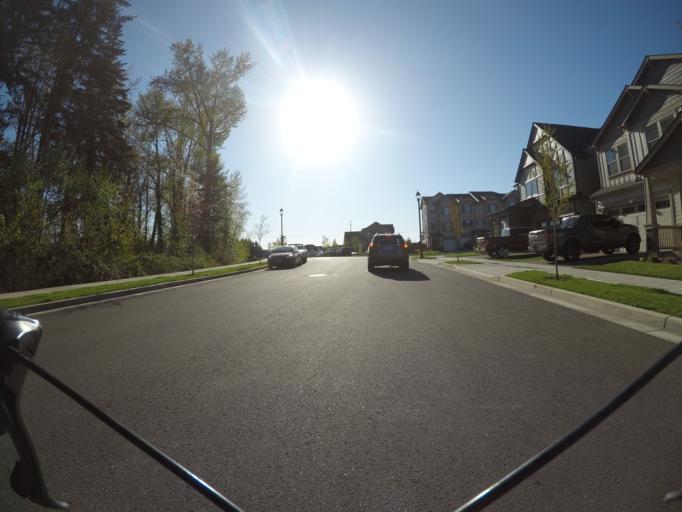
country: US
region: Oregon
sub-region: Washington County
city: King City
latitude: 45.4232
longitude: -122.8508
